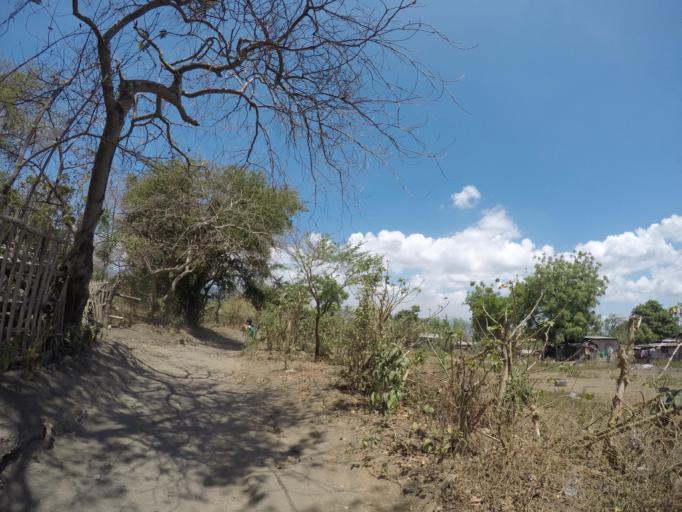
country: PH
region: Calabarzon
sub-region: Province of Batangas
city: Talisay
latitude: 14.0335
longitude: 121.0023
